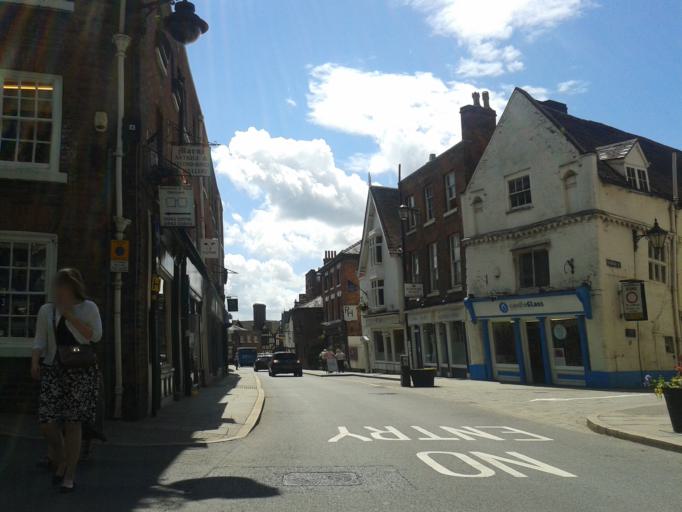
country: GB
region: England
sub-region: Shropshire
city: Shrewsbury
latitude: 52.7085
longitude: -2.7518
